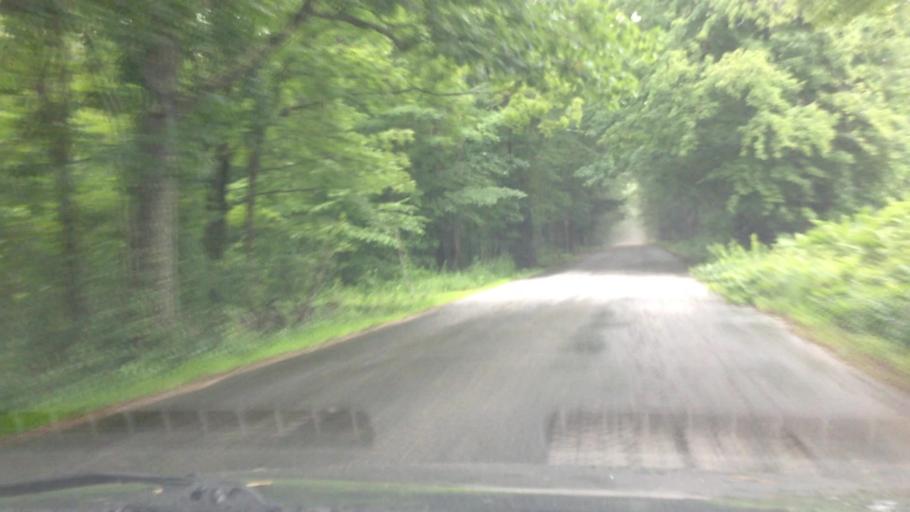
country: US
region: New Hampshire
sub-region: Cheshire County
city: Marlborough
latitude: 42.8904
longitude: -72.1927
